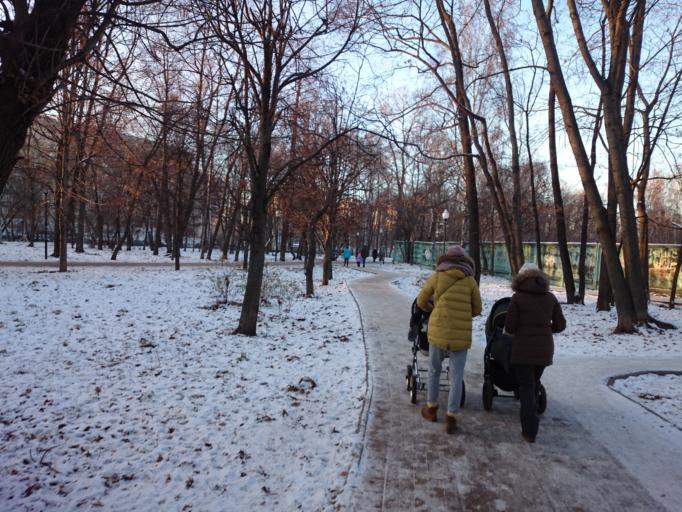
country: RU
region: Moscow
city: Sokol
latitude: 55.7868
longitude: 37.5150
